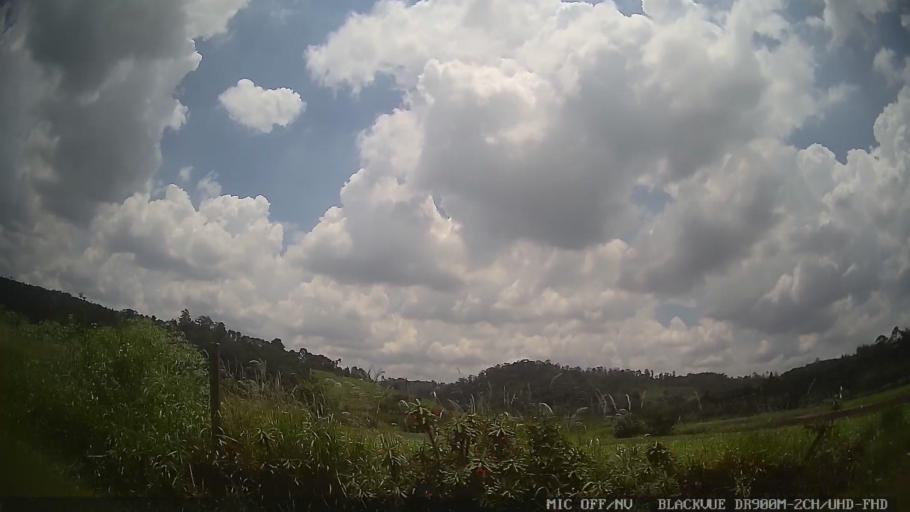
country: BR
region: Sao Paulo
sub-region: Ferraz De Vasconcelos
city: Ferraz de Vasconcelos
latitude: -23.5881
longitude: -46.3607
